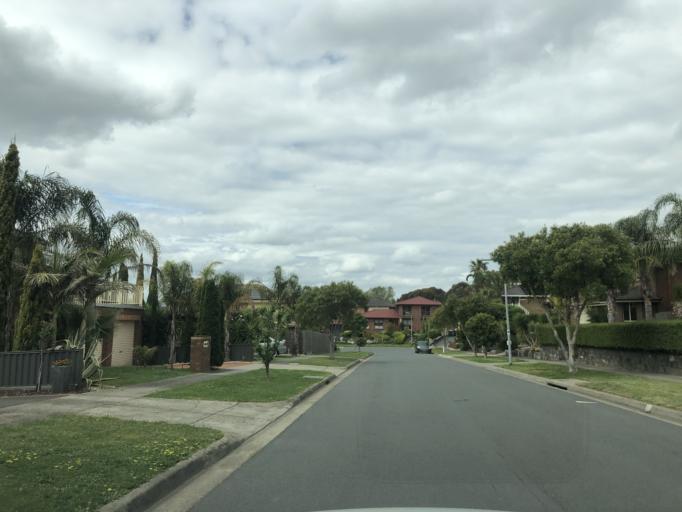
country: AU
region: Victoria
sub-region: Monash
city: Mulgrave
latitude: -37.9300
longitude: 145.1969
